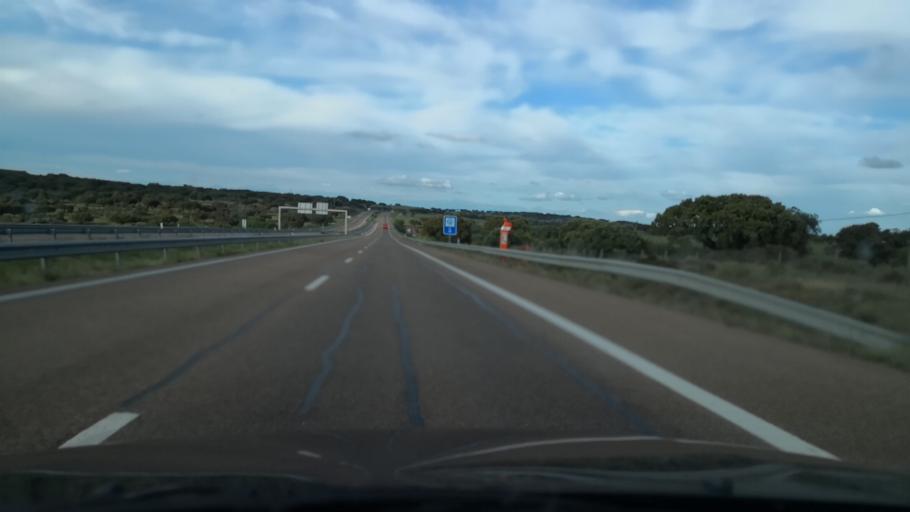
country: PT
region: Portalegre
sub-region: Elvas
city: Elvas
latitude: 38.8900
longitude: -7.2125
